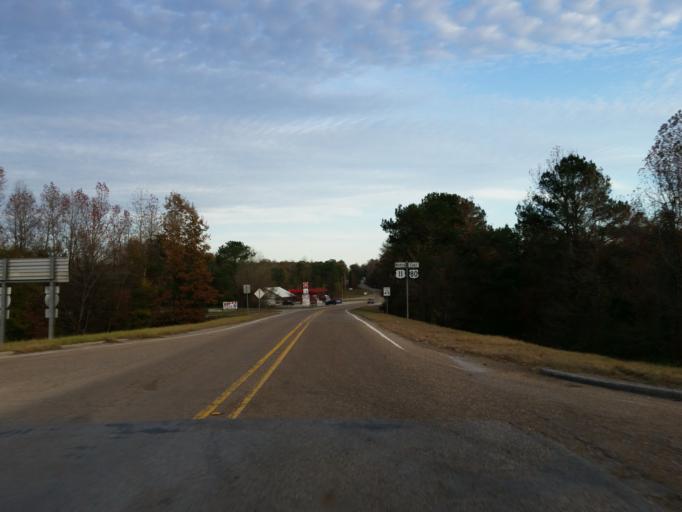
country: US
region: Alabama
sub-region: Sumter County
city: York
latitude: 32.4258
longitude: -88.4511
